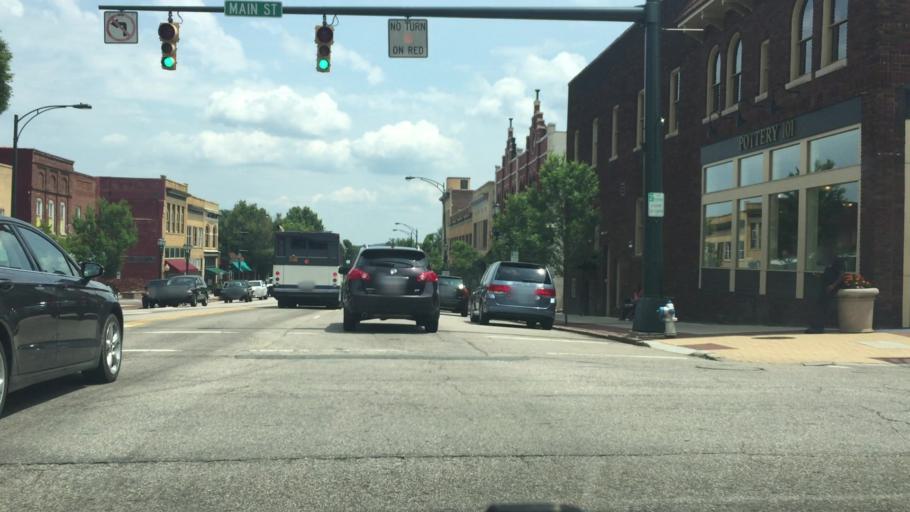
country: US
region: North Carolina
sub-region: Rowan County
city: Salisbury
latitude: 35.6674
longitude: -80.4699
